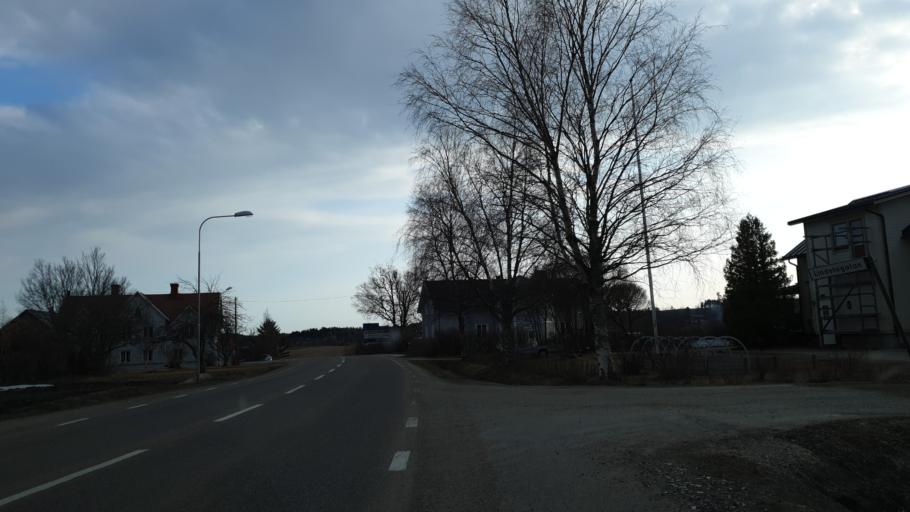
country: SE
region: Gaevleborg
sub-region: Nordanstigs Kommun
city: Bergsjoe
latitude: 61.9751
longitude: 17.2523
